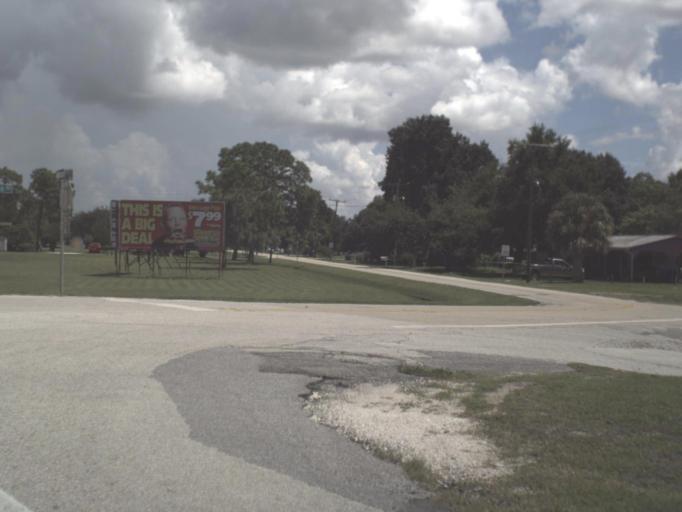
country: US
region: Florida
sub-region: Polk County
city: Auburndale
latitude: 28.0590
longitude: -81.7791
